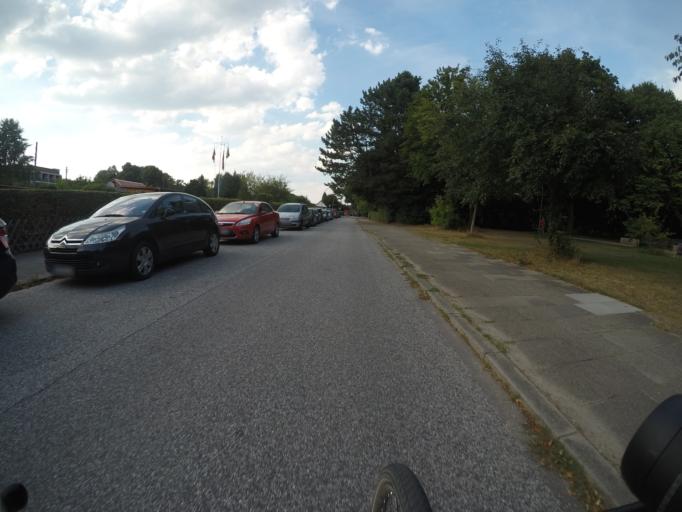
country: DE
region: Hamburg
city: Wandsbek
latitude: 53.5612
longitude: 10.1012
